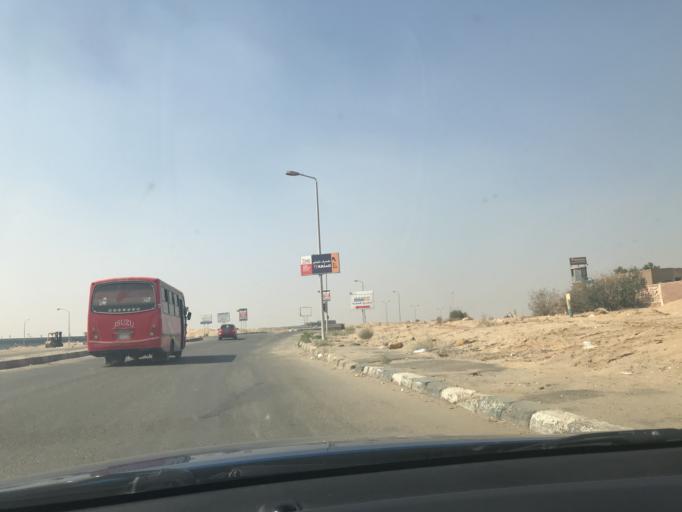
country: EG
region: Eastern Province
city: Bilbays
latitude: 30.2535
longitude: 31.7575
